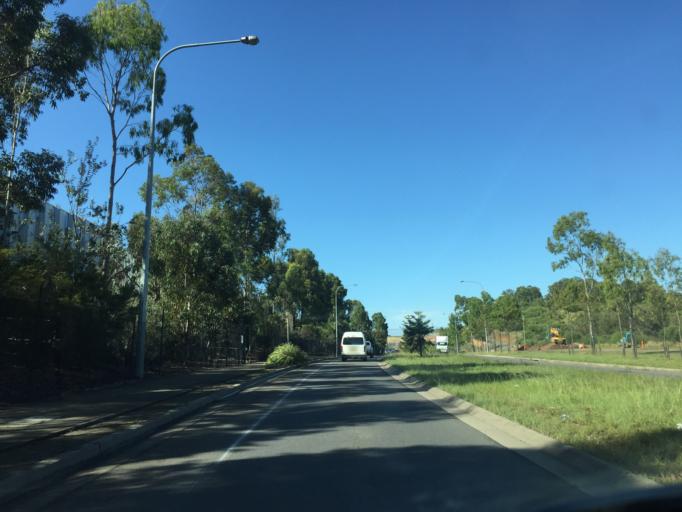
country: AU
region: New South Wales
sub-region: Holroyd
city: Girraween
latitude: -33.8164
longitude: 150.9206
